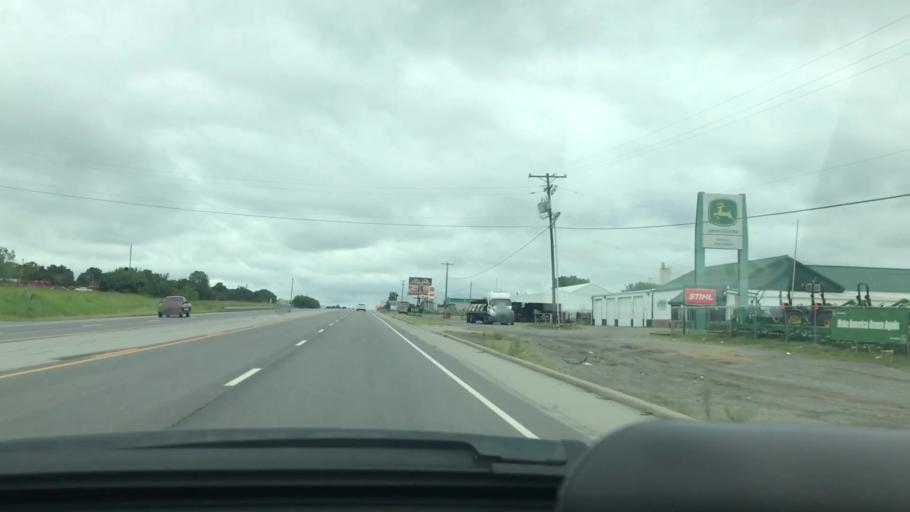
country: US
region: Oklahoma
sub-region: Pittsburg County
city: McAlester
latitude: 34.8726
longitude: -95.8026
